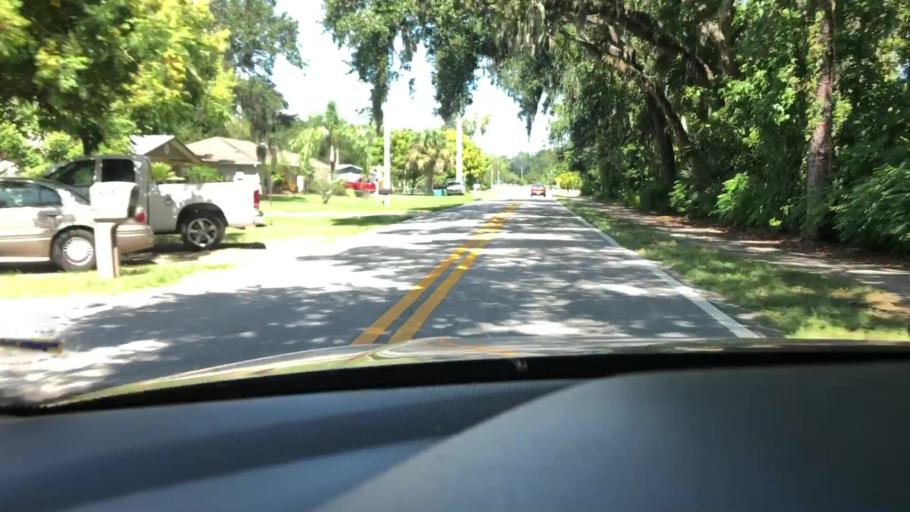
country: US
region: Florida
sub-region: Volusia County
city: Port Orange
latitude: 29.1275
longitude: -80.9930
